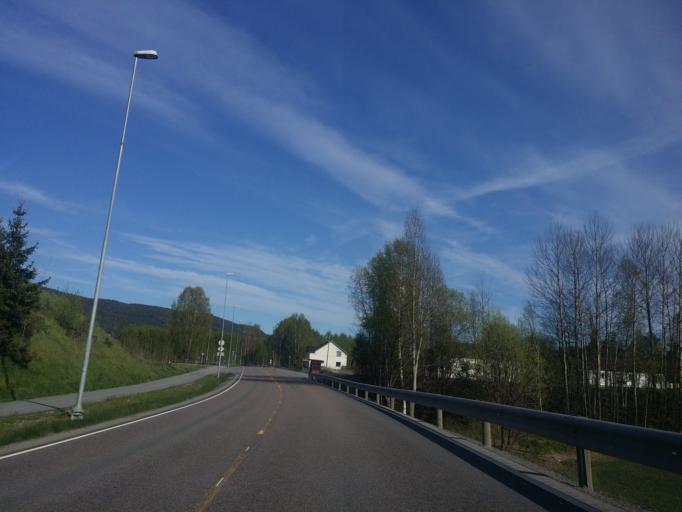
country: NO
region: Telemark
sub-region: Notodden
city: Notodden
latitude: 59.5928
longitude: 9.1458
